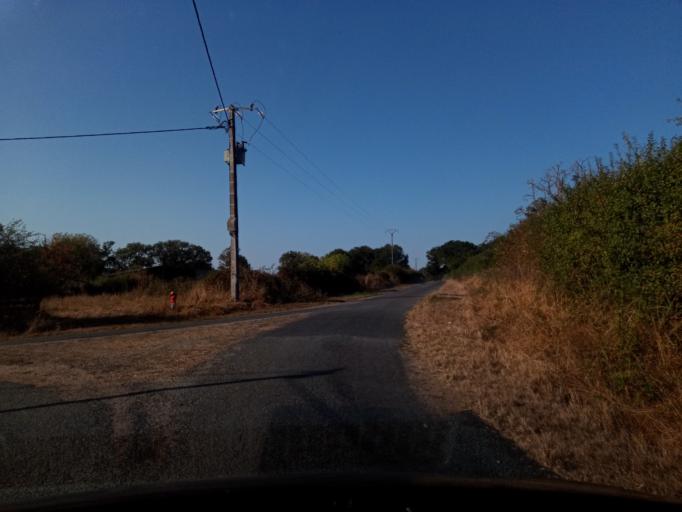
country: FR
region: Poitou-Charentes
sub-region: Departement de la Vienne
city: Saulge
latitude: 46.3765
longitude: 0.8650
